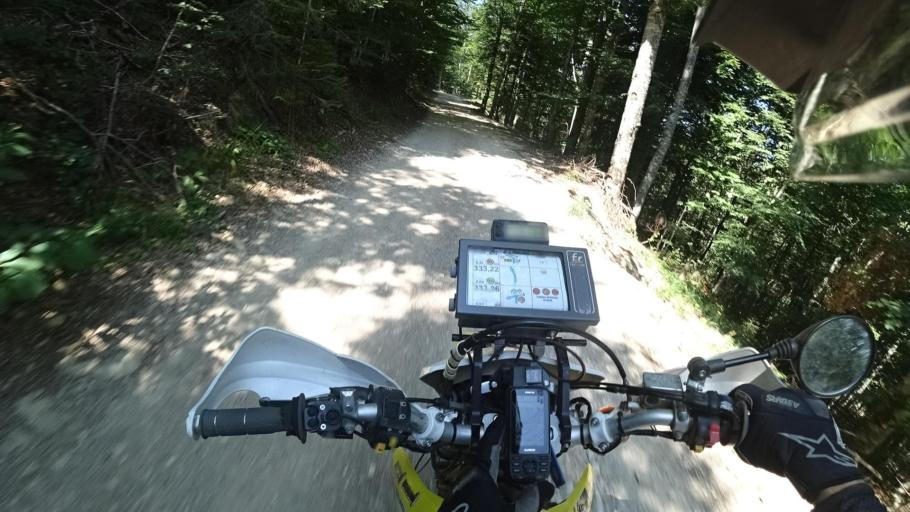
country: HR
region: Licko-Senjska
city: Popovaca
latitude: 44.5847
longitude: 15.1891
